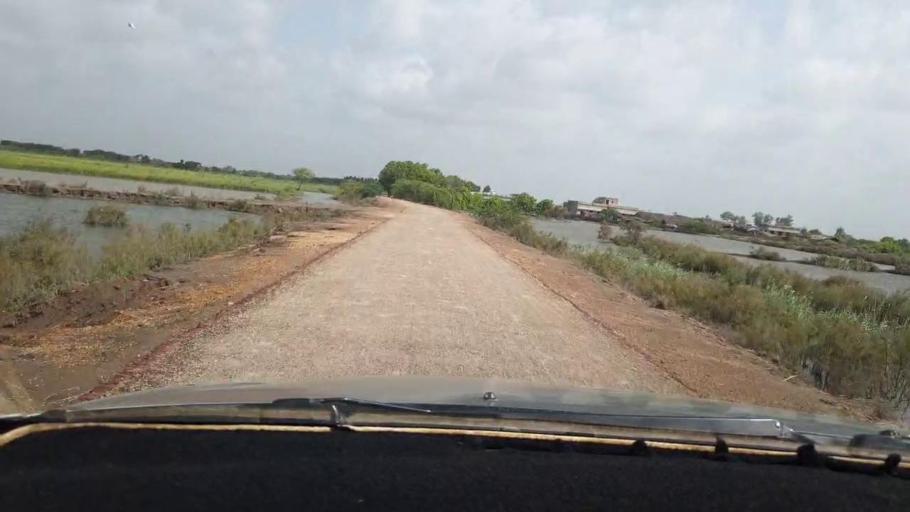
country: PK
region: Sindh
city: Tando Bago
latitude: 24.7878
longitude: 69.0284
